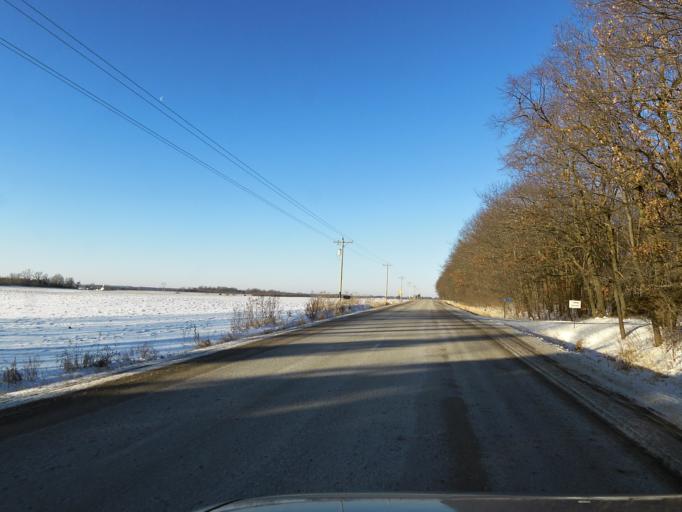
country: US
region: Minnesota
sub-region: Scott County
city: Jordan
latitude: 44.6597
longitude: -93.5662
